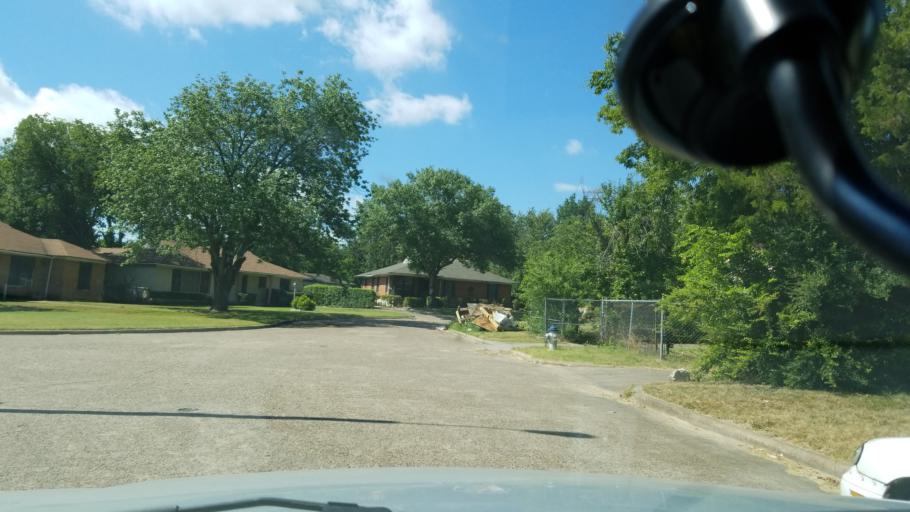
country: US
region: Texas
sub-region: Dallas County
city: Cockrell Hill
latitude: 32.6818
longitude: -96.8121
